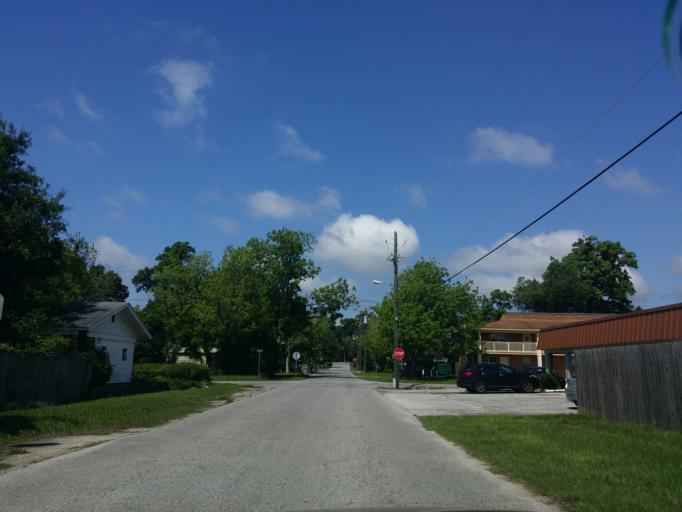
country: US
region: Florida
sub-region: Escambia County
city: Warrington
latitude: 30.3866
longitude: -87.2747
